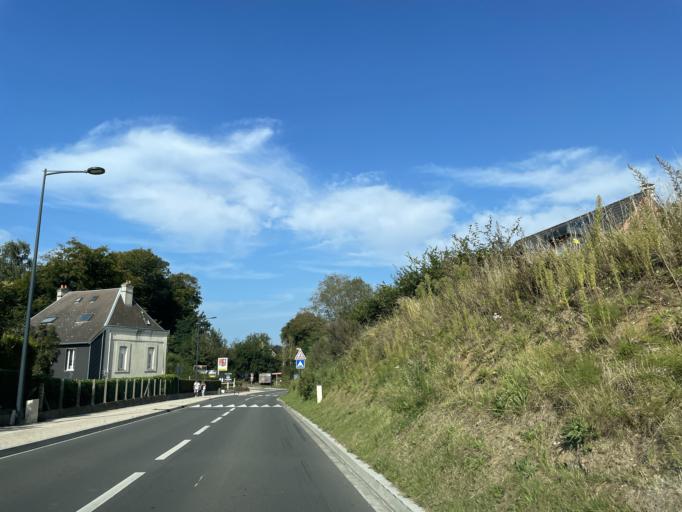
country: FR
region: Haute-Normandie
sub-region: Departement de la Seine-Maritime
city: Le Treport
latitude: 50.0509
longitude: 1.3674
